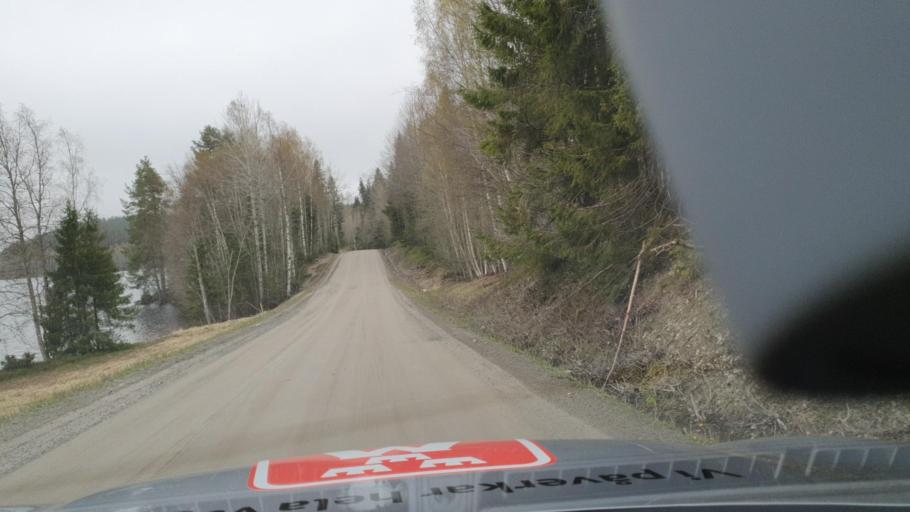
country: SE
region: Vaesternorrland
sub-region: OErnskoeldsviks Kommun
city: Husum
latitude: 63.6371
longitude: 19.0588
